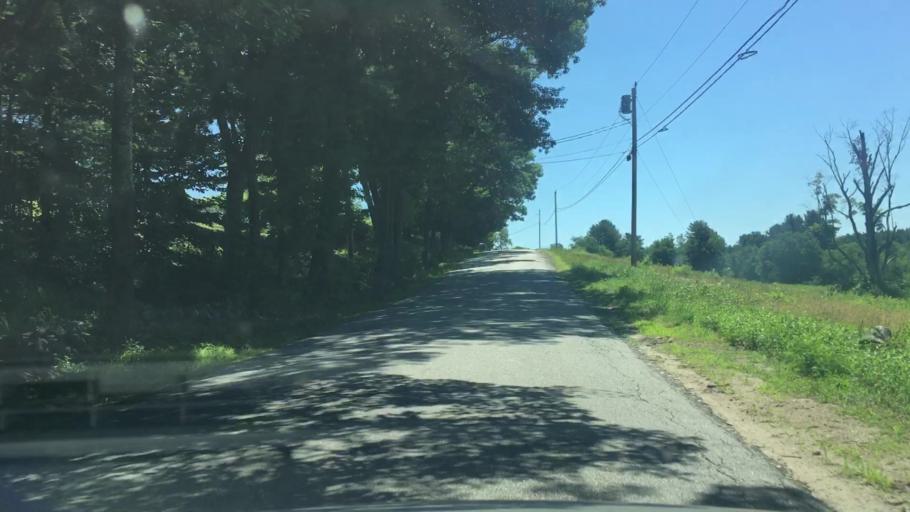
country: US
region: New Hampshire
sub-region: Merrimack County
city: Hopkinton
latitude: 43.2199
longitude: -71.6759
